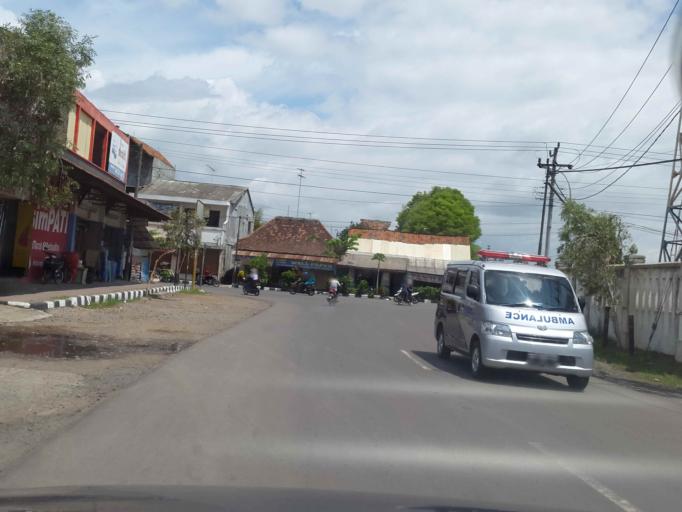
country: ID
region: Central Java
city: Kutoarjo
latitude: -7.7258
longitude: 109.9096
